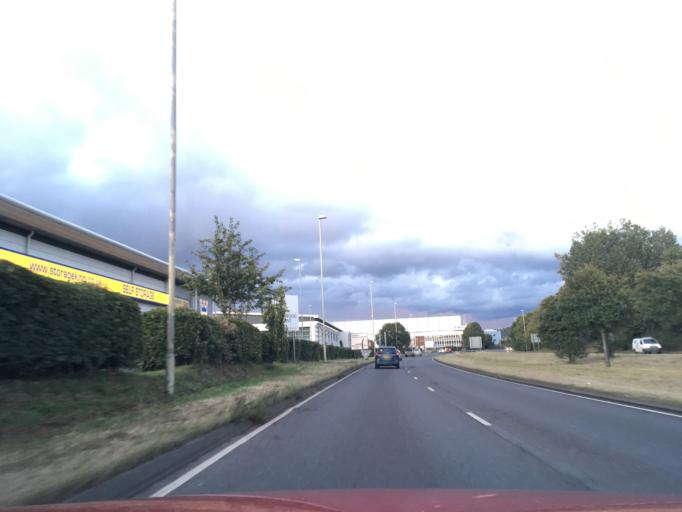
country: GB
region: England
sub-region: Gloucestershire
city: Barnwood
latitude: 51.8651
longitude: -2.2118
